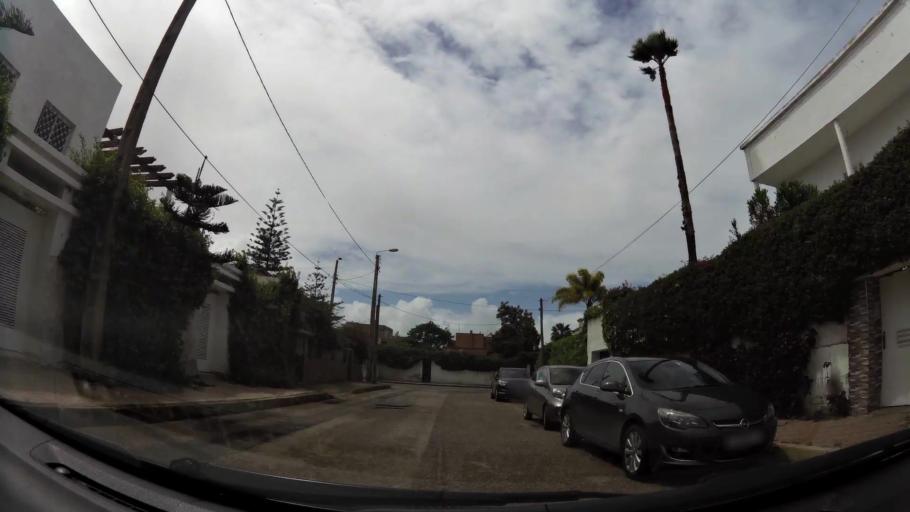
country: MA
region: Grand Casablanca
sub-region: Casablanca
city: Casablanca
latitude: 33.5662
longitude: -7.6304
